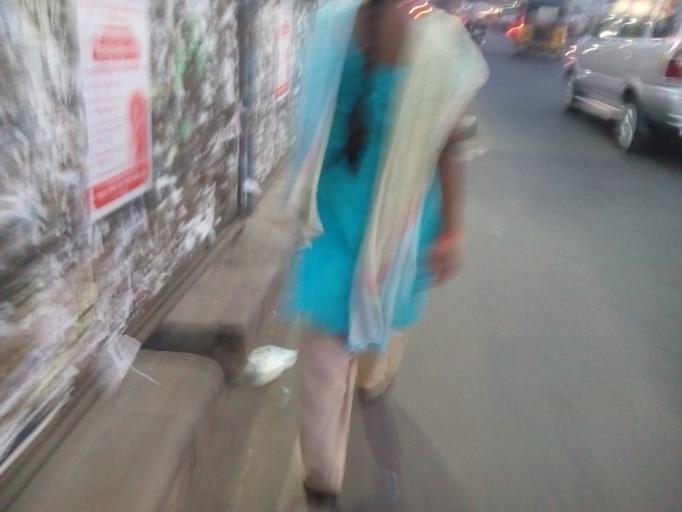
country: IN
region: Andhra Pradesh
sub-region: Guntur
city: Guntur
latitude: 16.3014
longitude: 80.4395
